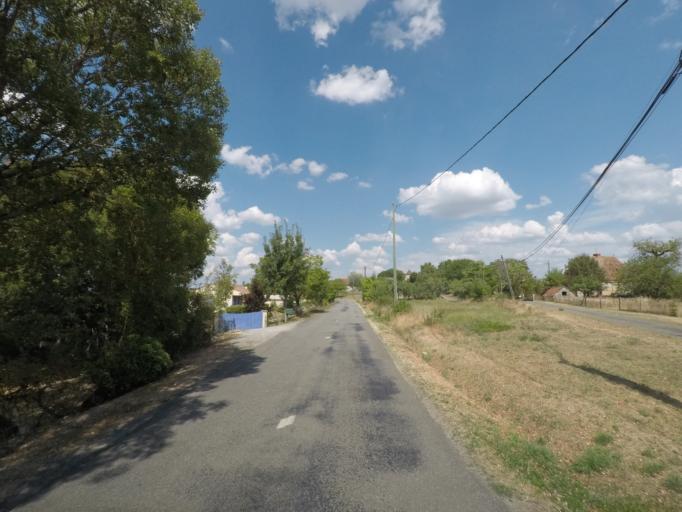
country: FR
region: Midi-Pyrenees
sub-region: Departement du Lot
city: Cahors
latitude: 44.5891
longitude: 1.5802
